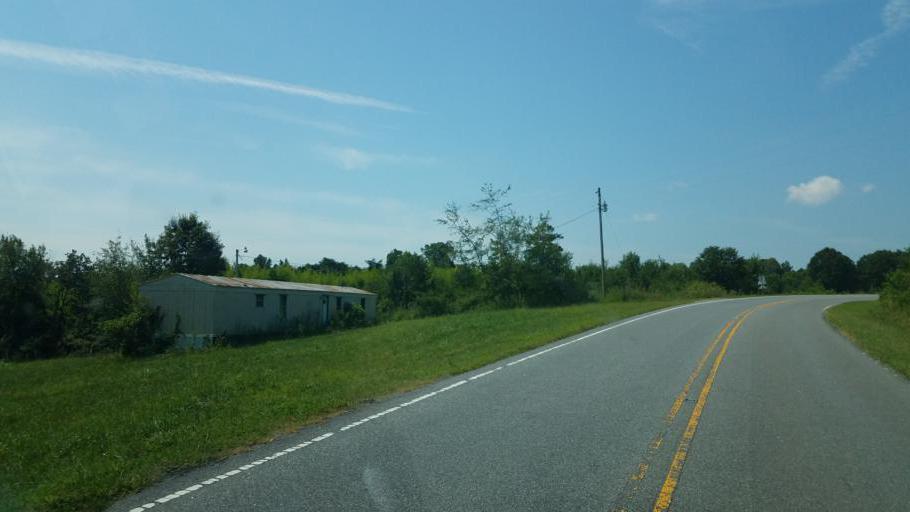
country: US
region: North Carolina
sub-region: Burke County
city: Icard
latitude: 35.5685
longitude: -81.5096
